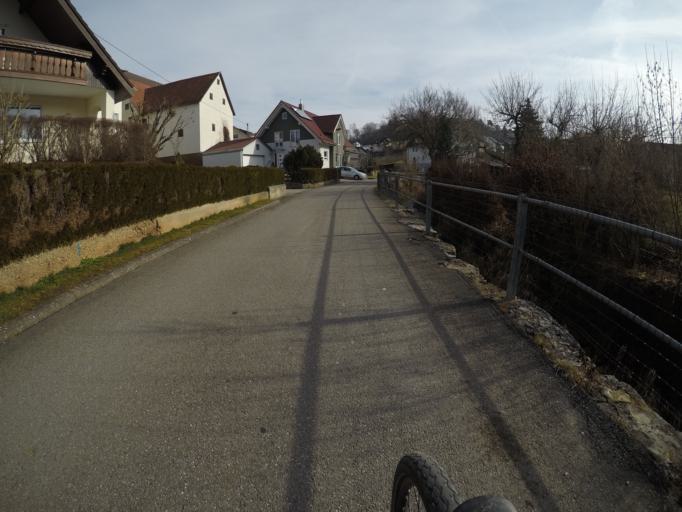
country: DE
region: Baden-Wuerttemberg
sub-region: Karlsruhe Region
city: Wildberg
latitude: 48.6151
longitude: 8.7810
